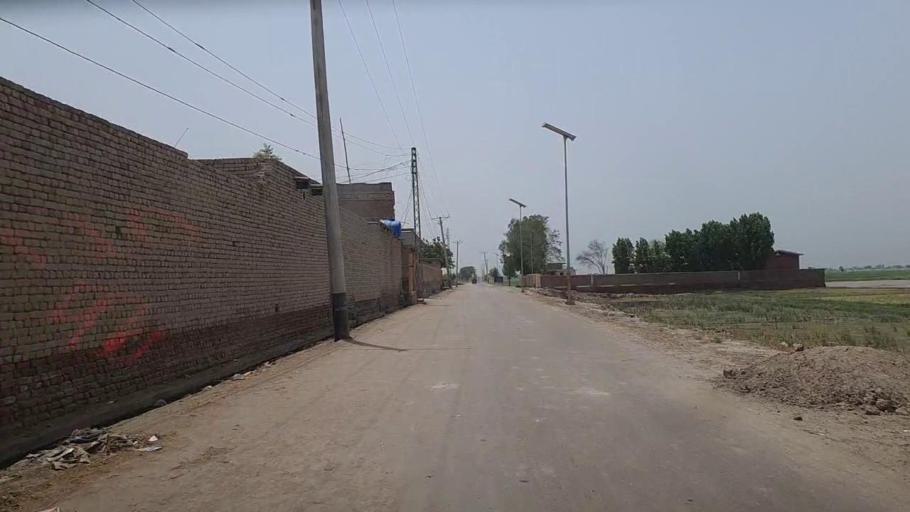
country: PK
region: Sindh
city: Sita Road
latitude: 27.0594
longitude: 67.9037
